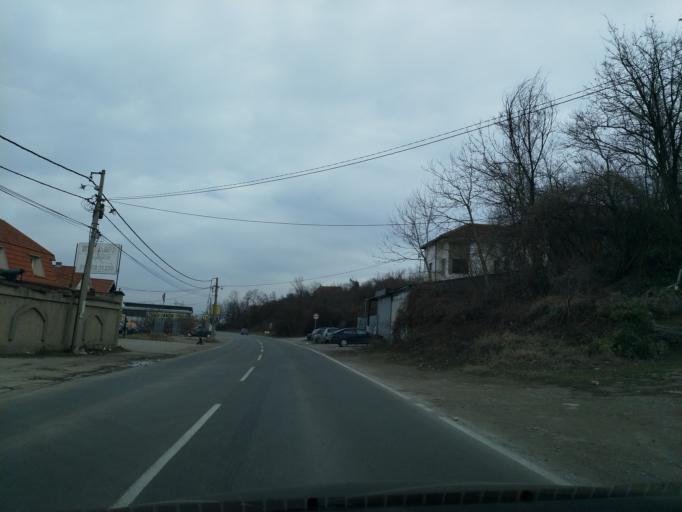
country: RS
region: Central Serbia
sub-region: Belgrade
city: Zvezdara
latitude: 44.7287
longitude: 20.5814
